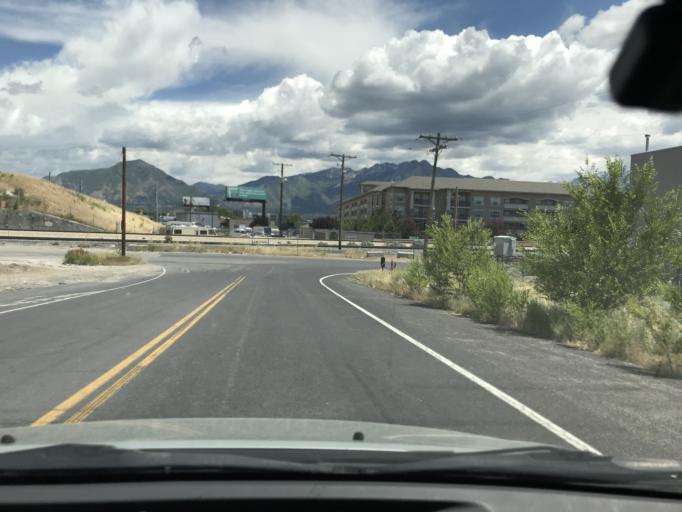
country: US
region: Utah
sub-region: Salt Lake County
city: Centerfield
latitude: 40.6862
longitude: -111.9004
